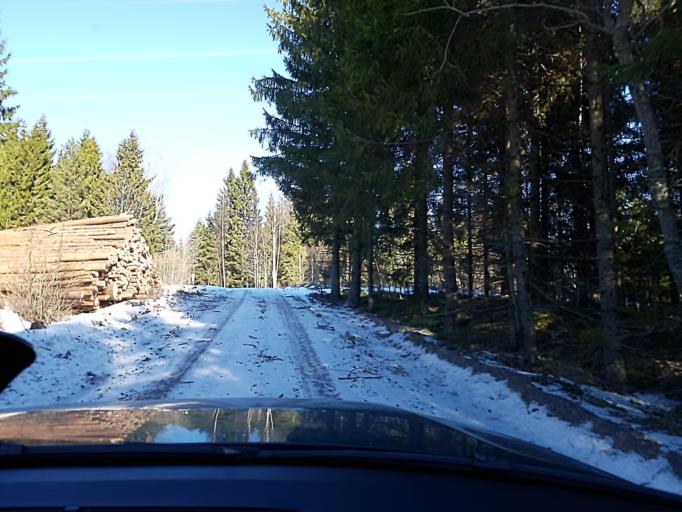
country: FI
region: Uusimaa
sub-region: Helsinki
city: Karjalohja
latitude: 60.2020
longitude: 23.7023
